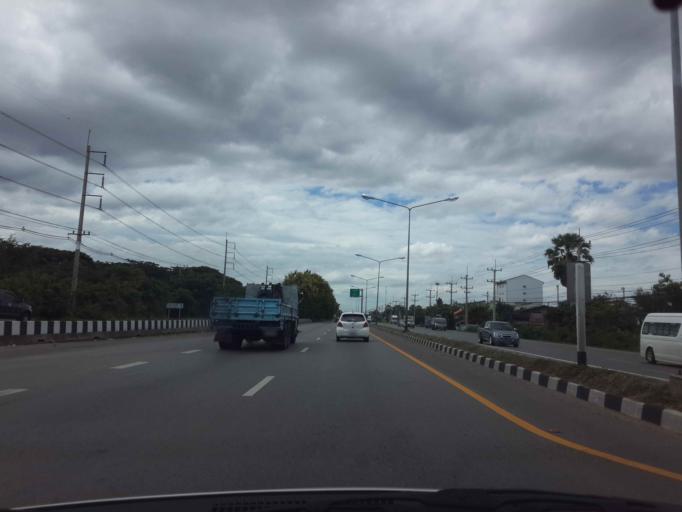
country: TH
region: Phetchaburi
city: Khao Yoi
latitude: 13.1543
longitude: 99.8497
